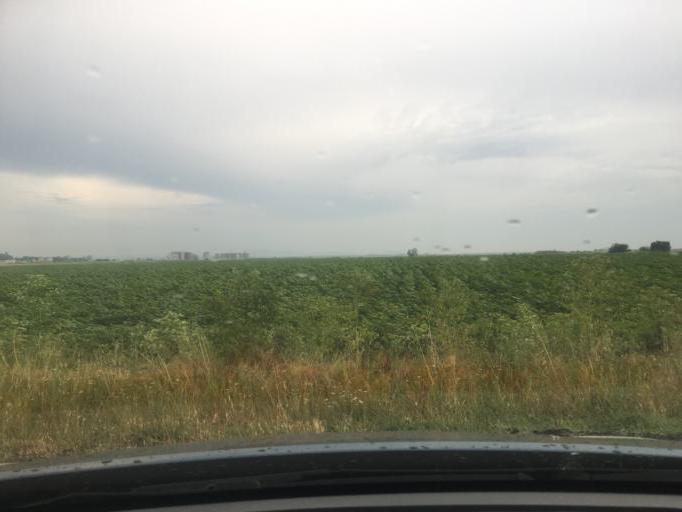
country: BG
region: Burgas
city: Aheloy
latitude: 42.6464
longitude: 27.6334
